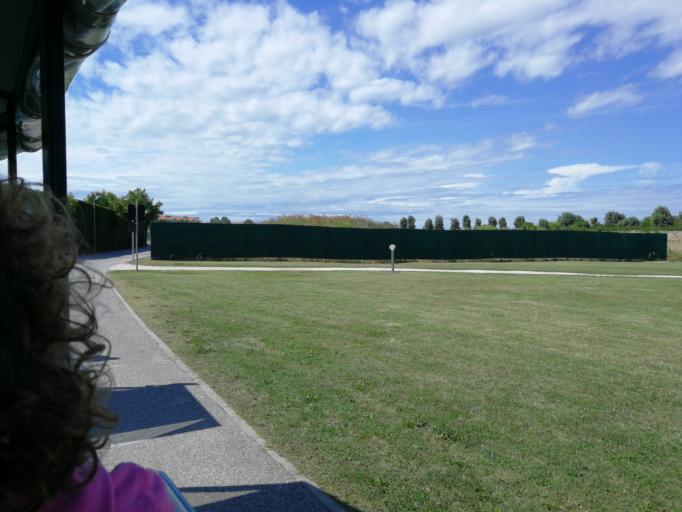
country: IT
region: Veneto
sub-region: Provincia di Venezia
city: Caorle
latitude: 45.5761
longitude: 12.8272
